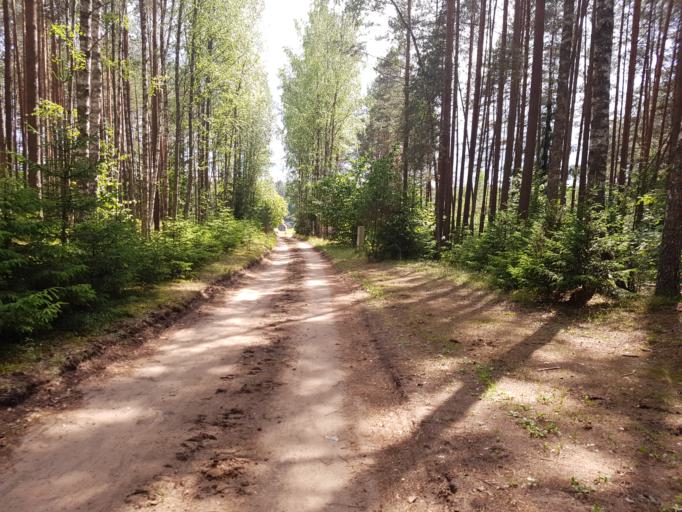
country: LT
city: Svencioneliai
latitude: 55.2360
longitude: 25.8081
